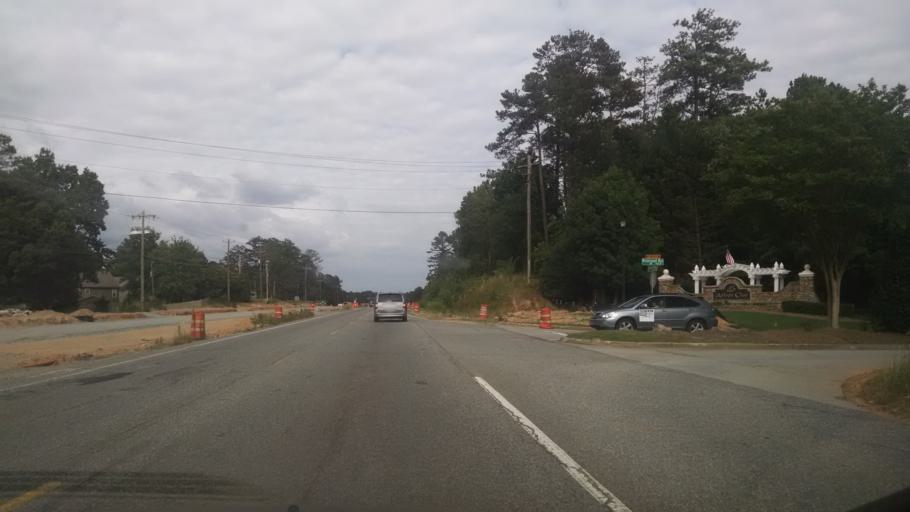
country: US
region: Georgia
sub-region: Gwinnett County
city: Sugar Hill
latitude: 34.1120
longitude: -84.0661
